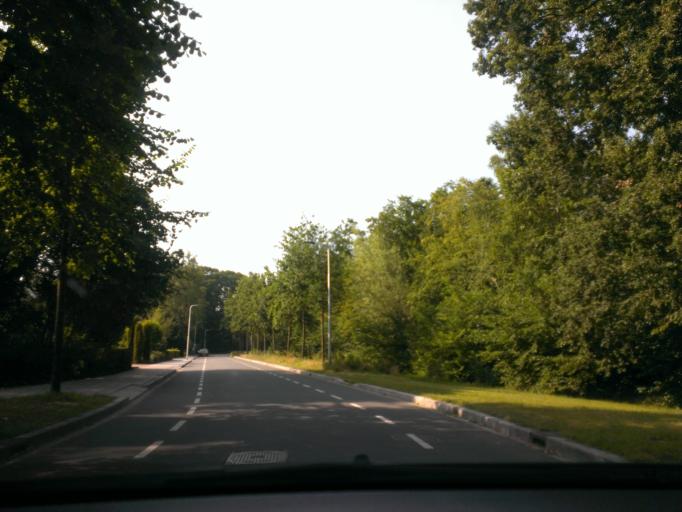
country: NL
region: Gelderland
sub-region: Gemeente Epe
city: Epe
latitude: 52.3435
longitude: 5.9913
